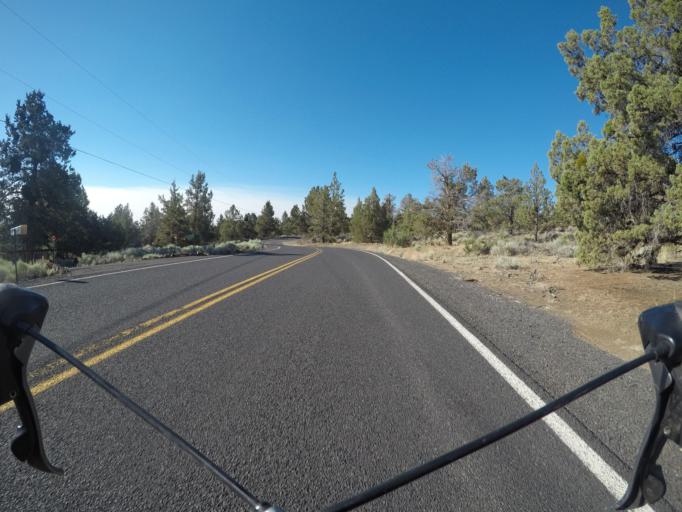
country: US
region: Oregon
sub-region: Deschutes County
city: Bend
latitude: 44.1789
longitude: -121.2662
